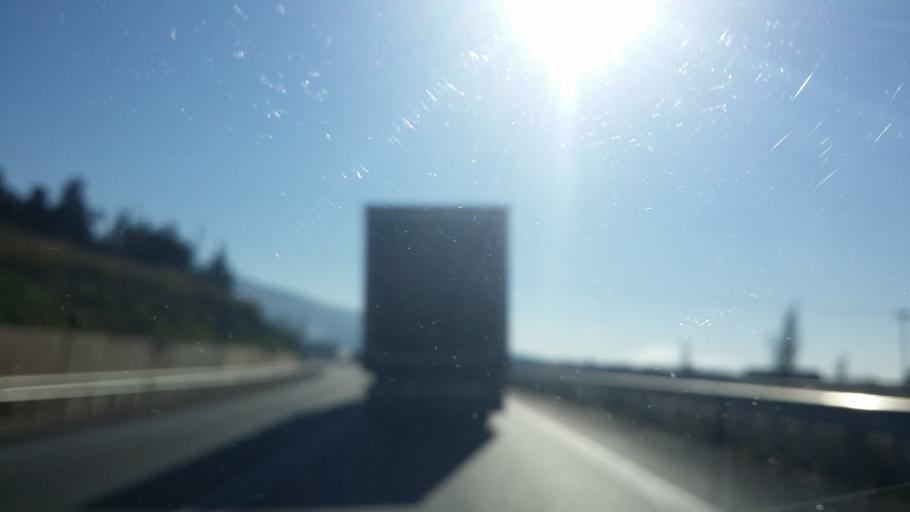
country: GR
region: West Greece
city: Aitoliko
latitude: 38.4424
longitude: 21.3743
